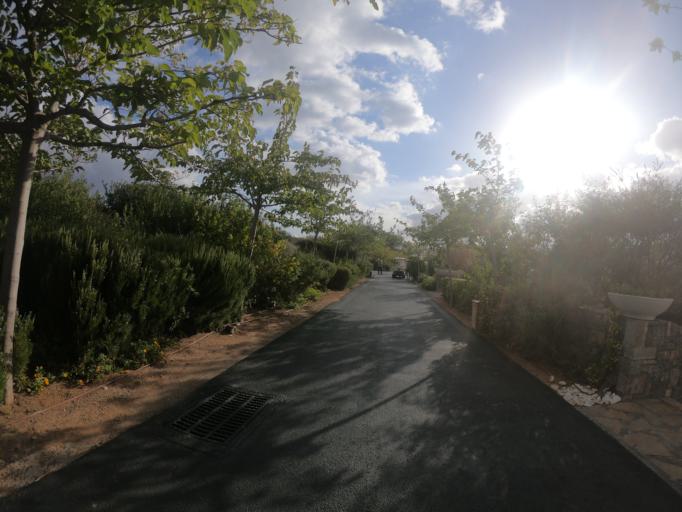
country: GR
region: Attica
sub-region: Nomarchia Anatolikis Attikis
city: Saronida
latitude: 37.7763
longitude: 23.8870
